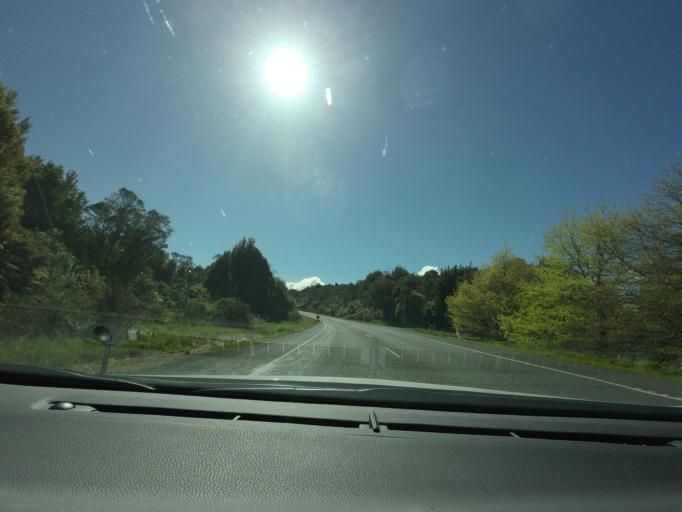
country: NZ
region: Bay of Plenty
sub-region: Rotorua District
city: Rotorua
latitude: -38.0704
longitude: 176.1192
